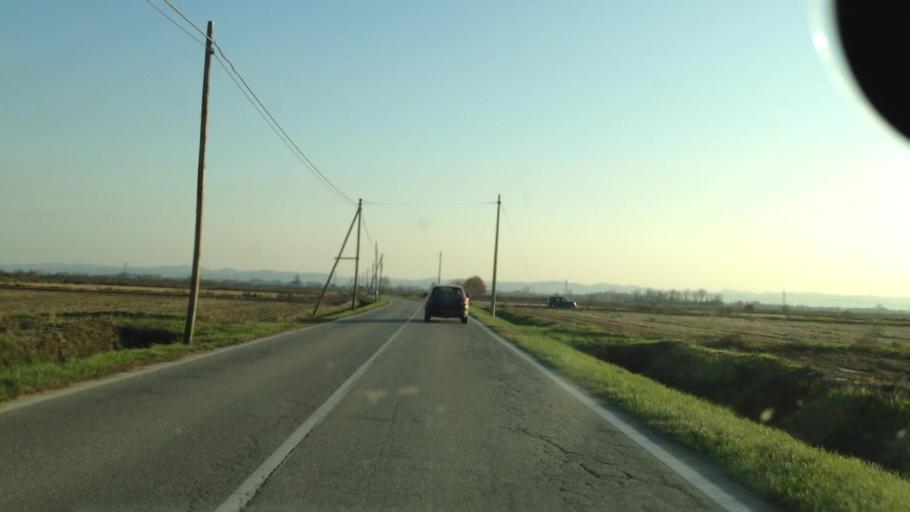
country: IT
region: Piedmont
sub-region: Provincia di Vercelli
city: Livorno Ferraris
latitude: 45.2604
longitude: 8.0845
